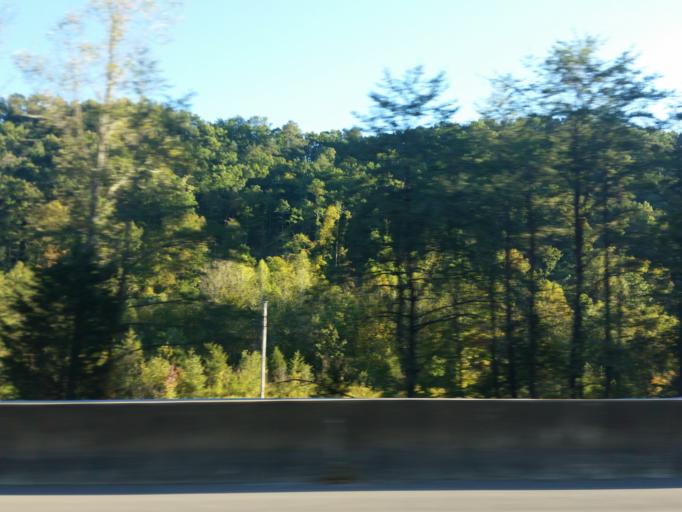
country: US
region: Tennessee
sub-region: Grainger County
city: Bean Station
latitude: 36.3608
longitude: -83.3435
